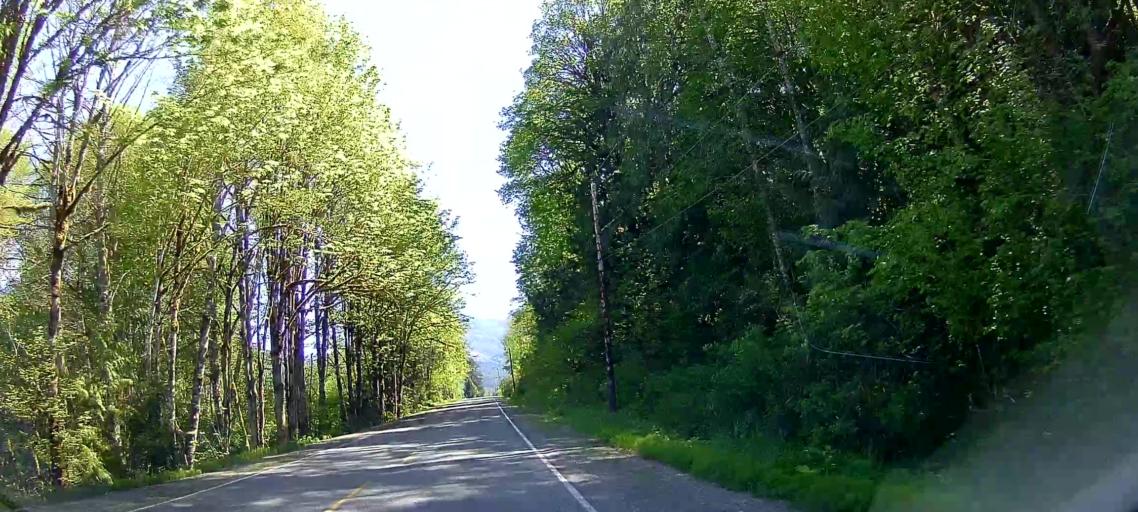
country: US
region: Washington
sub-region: Snohomish County
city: Darrington
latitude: 48.5184
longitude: -121.7423
